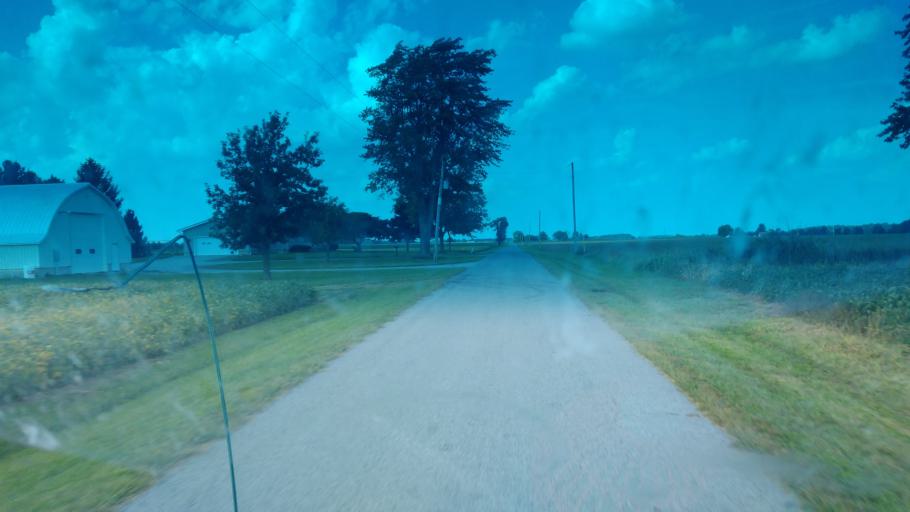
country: US
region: Ohio
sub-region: Hancock County
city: Arlington
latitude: 40.8568
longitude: -83.5855
